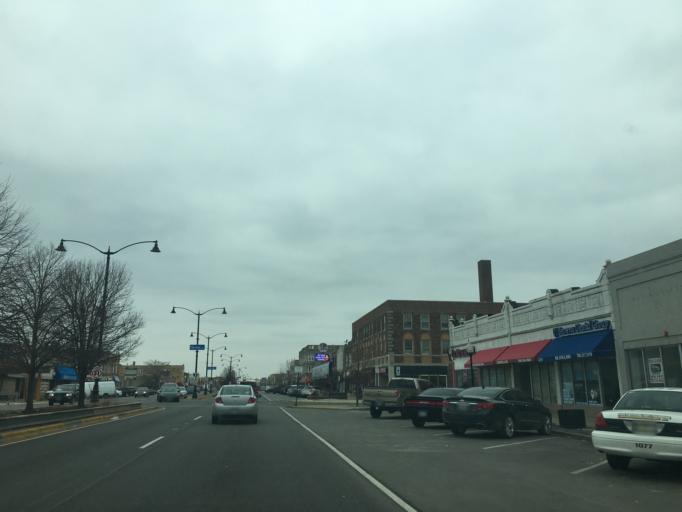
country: US
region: Illinois
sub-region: Cook County
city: Berwyn
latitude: 41.8508
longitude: -87.7795
